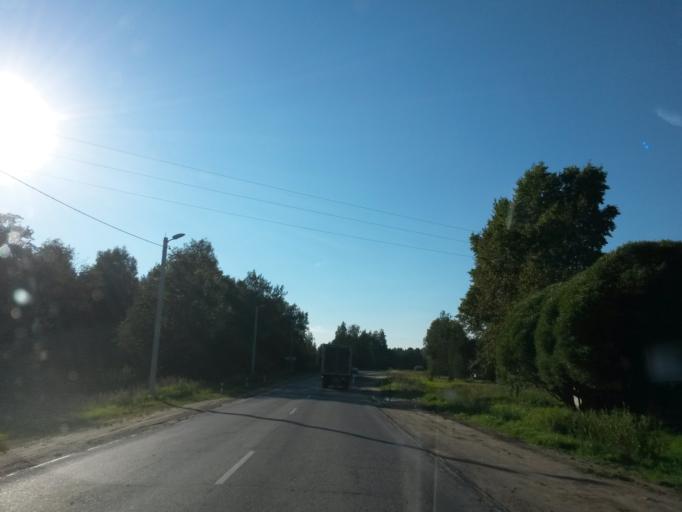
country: RU
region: Ivanovo
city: Novo-Talitsy
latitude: 57.0681
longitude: 40.6965
